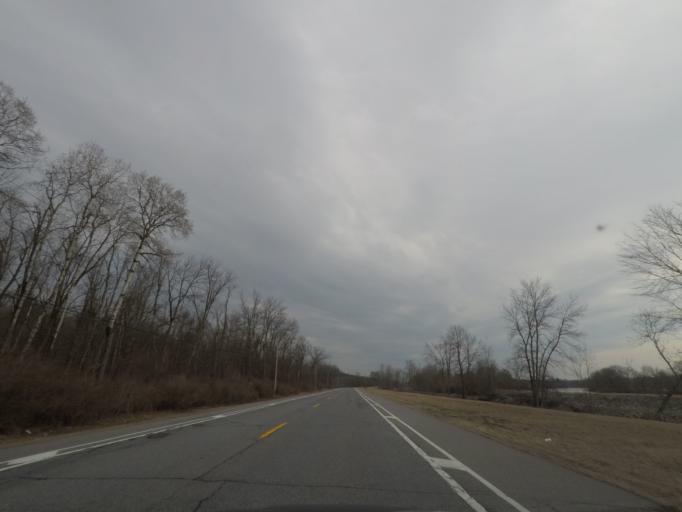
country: US
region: New York
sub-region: Washington County
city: Fort Edward
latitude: 43.1858
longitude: -73.5795
